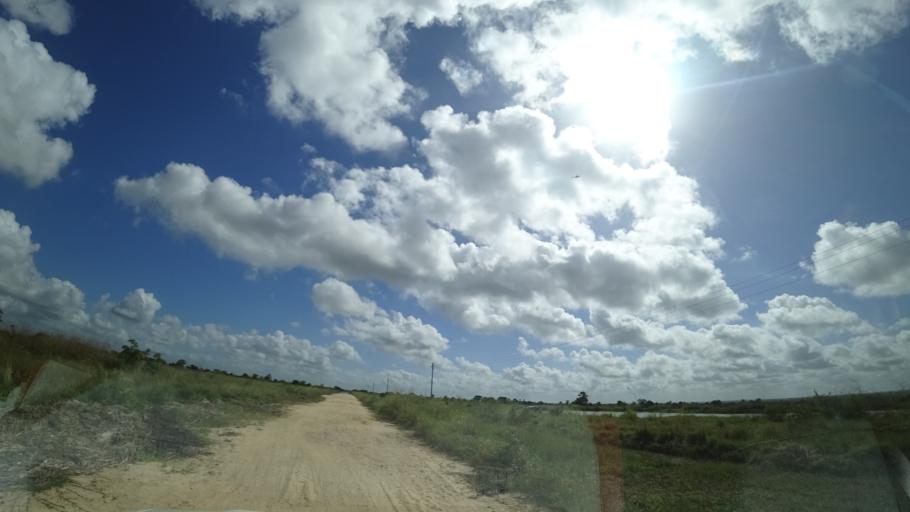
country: MZ
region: Sofala
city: Dondo
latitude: -19.4490
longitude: 34.5623
